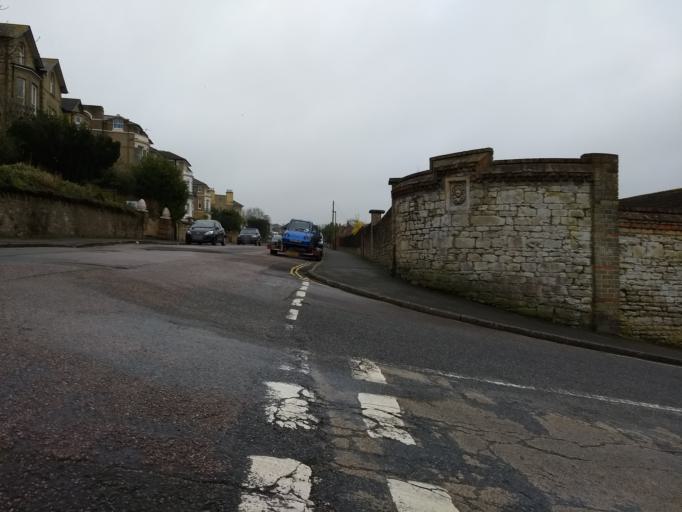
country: GB
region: England
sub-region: Isle of Wight
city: Ryde
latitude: 50.7258
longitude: -1.1506
